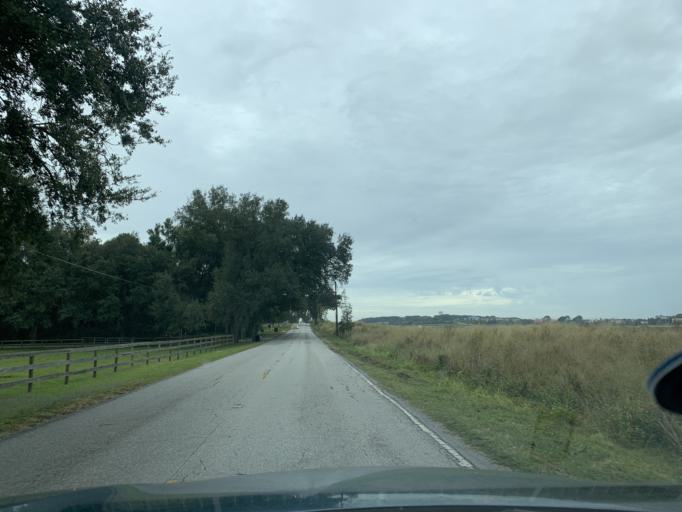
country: US
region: Florida
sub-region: Pasco County
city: Zephyrhills North
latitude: 28.2782
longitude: -82.1798
